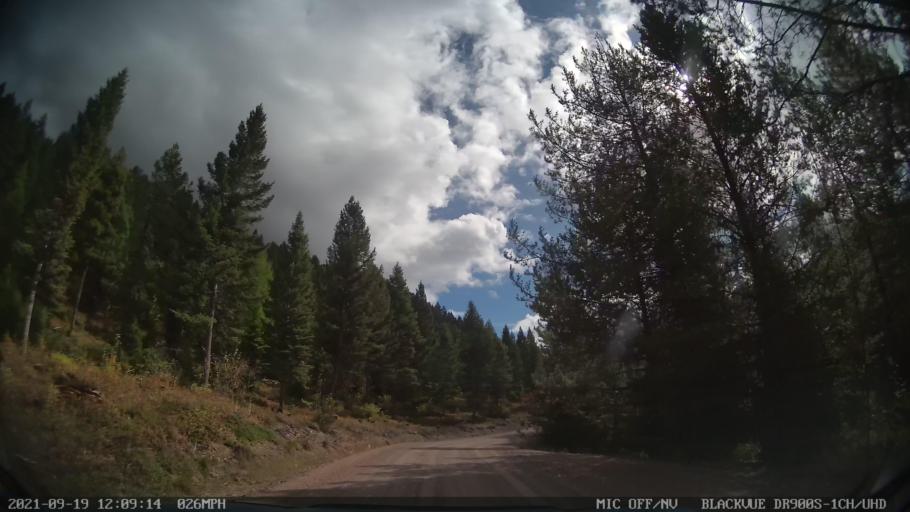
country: US
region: Montana
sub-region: Missoula County
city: Seeley Lake
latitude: 47.1844
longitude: -113.3926
